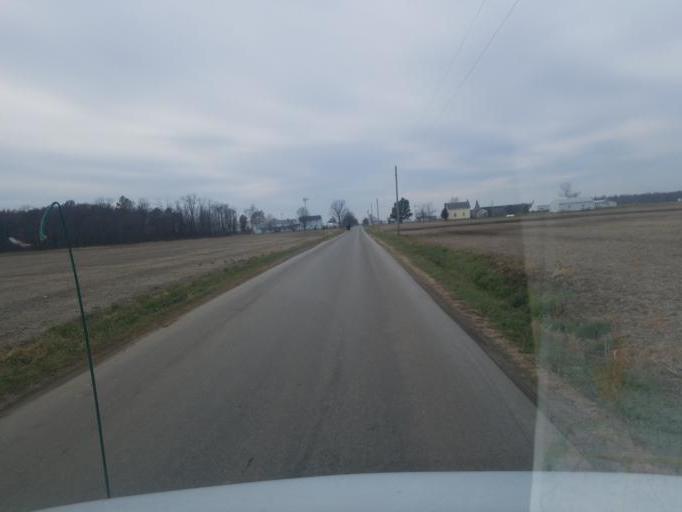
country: US
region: Indiana
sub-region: Adams County
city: Geneva
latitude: 40.6151
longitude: -84.8832
